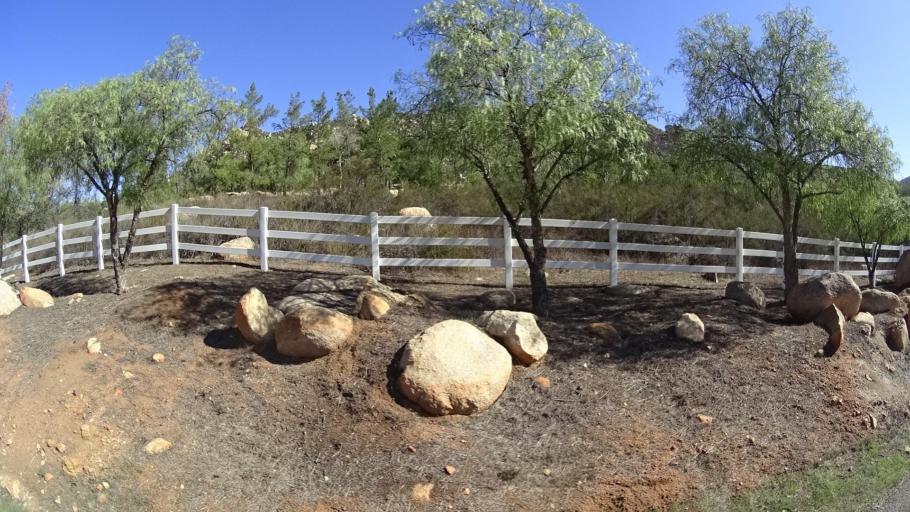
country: US
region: California
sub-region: San Diego County
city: Jamul
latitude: 32.7140
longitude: -116.8006
